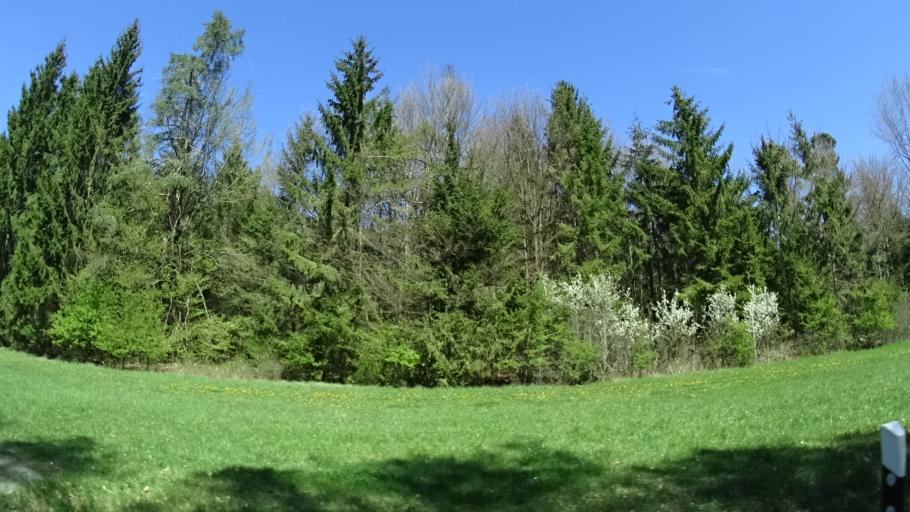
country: DE
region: Bavaria
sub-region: Upper Palatinate
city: Illschwang
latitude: 49.4242
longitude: 11.6796
